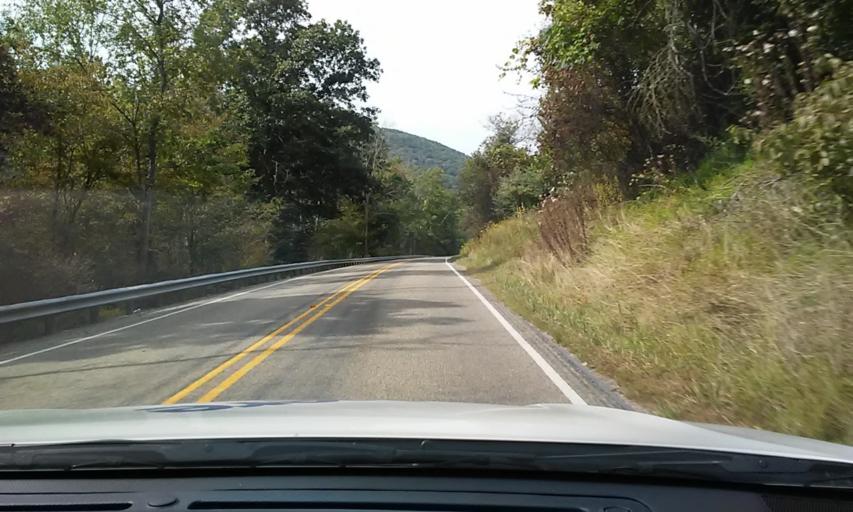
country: US
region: Pennsylvania
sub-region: Cameron County
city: Emporium
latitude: 41.3459
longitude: -78.2725
